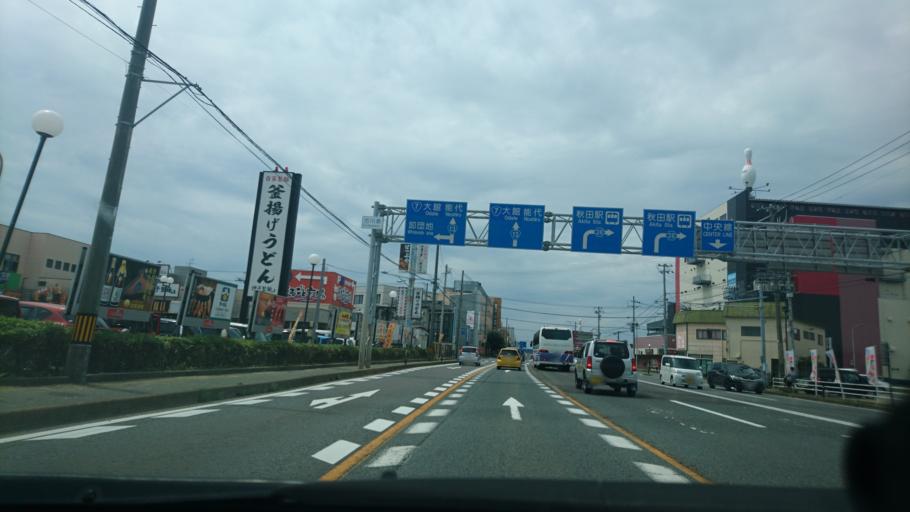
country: JP
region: Akita
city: Akita
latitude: 39.7006
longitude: 140.1112
